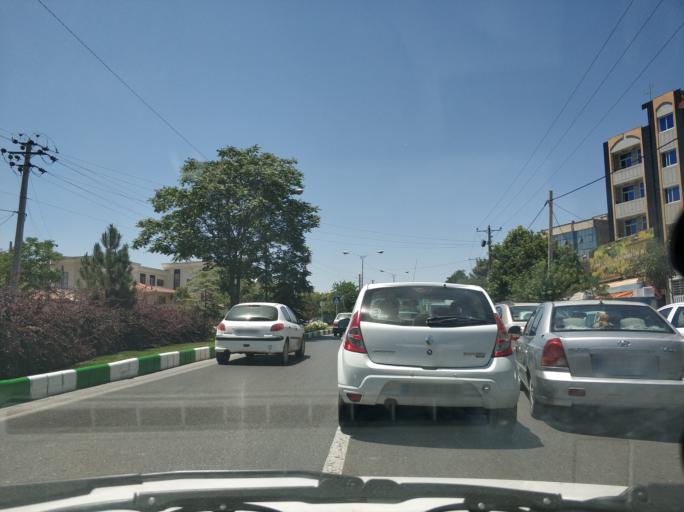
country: IR
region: Razavi Khorasan
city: Mashhad
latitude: 36.3130
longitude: 59.4922
